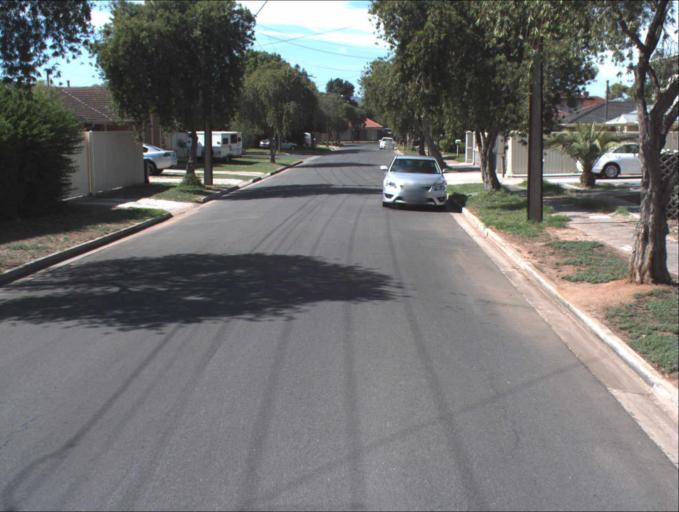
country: AU
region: South Australia
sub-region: Port Adelaide Enfield
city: Klemzig
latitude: -34.8787
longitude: 138.6417
